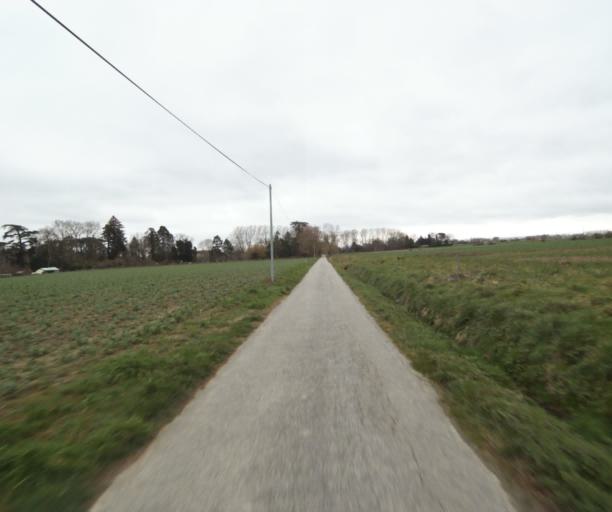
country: FR
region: Midi-Pyrenees
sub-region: Departement de l'Ariege
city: Saverdun
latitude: 43.1881
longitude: 1.6021
